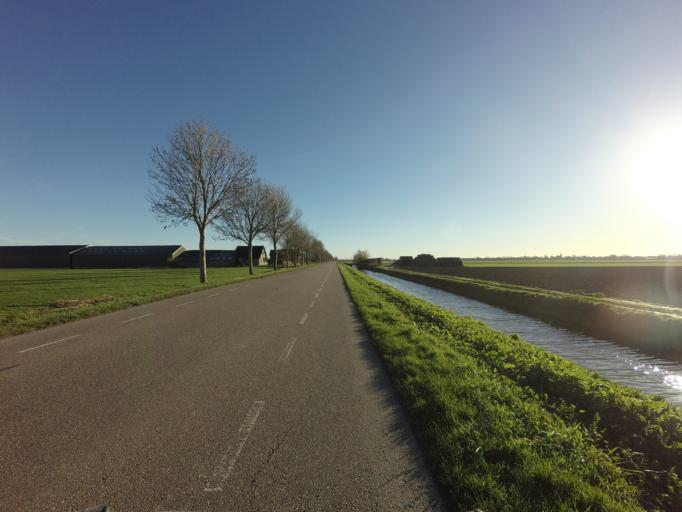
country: NL
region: South Holland
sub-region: Gemeente Nieuwkoop
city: Nieuwkoop
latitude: 52.1922
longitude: 4.7892
